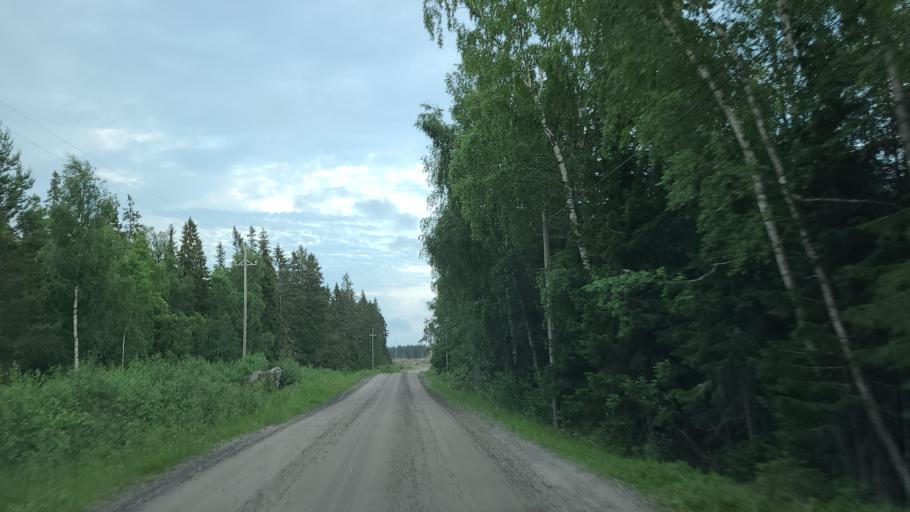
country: FI
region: Ostrobothnia
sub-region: Vaasa
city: Replot
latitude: 63.3210
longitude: 21.1442
